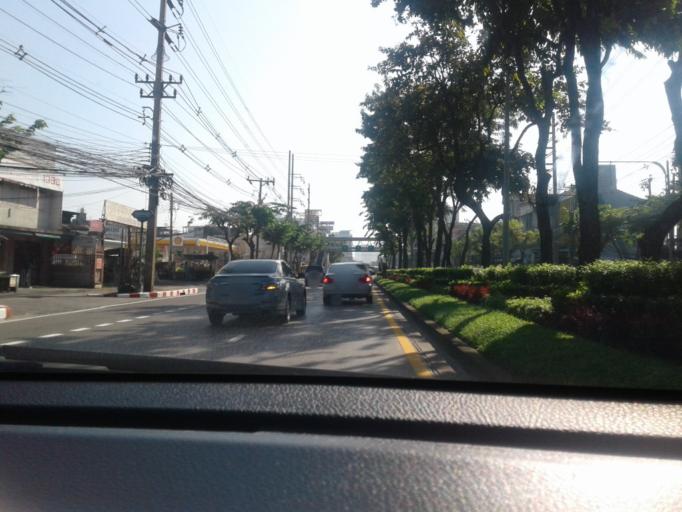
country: TH
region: Bangkok
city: Thon Buri
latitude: 13.7283
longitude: 100.4815
